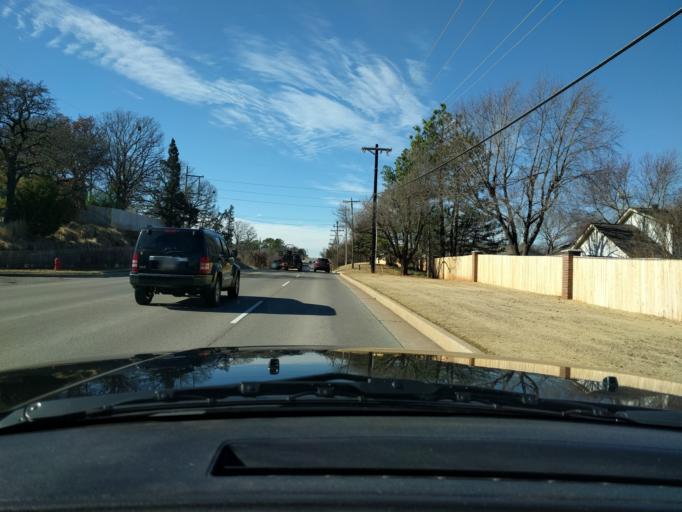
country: US
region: Oklahoma
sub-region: Oklahoma County
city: Edmond
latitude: 35.6383
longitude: -97.4505
